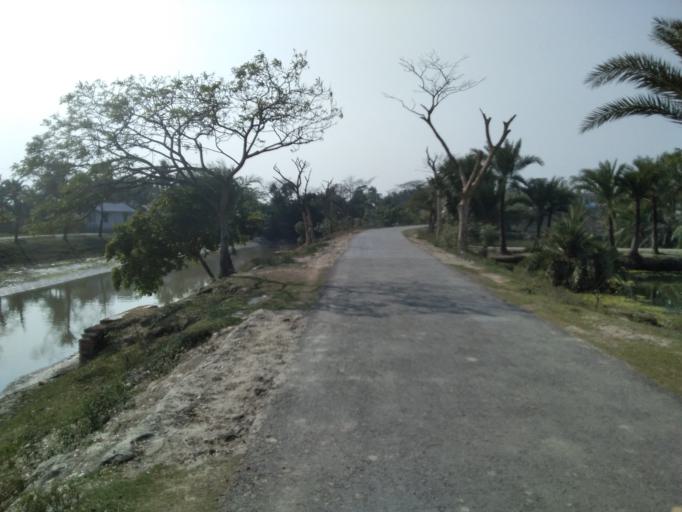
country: IN
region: West Bengal
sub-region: North 24 Parganas
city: Taki
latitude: 22.6370
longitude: 89.0023
